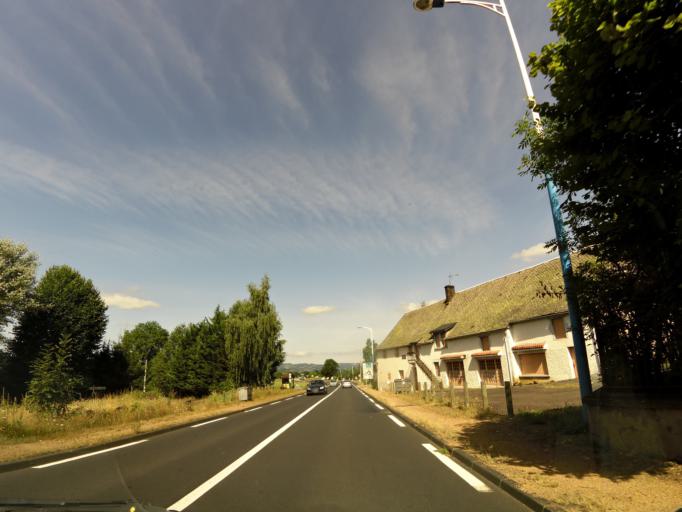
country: FR
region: Auvergne
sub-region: Departement du Puy-de-Dome
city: Aydat
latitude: 45.7268
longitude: 2.8937
